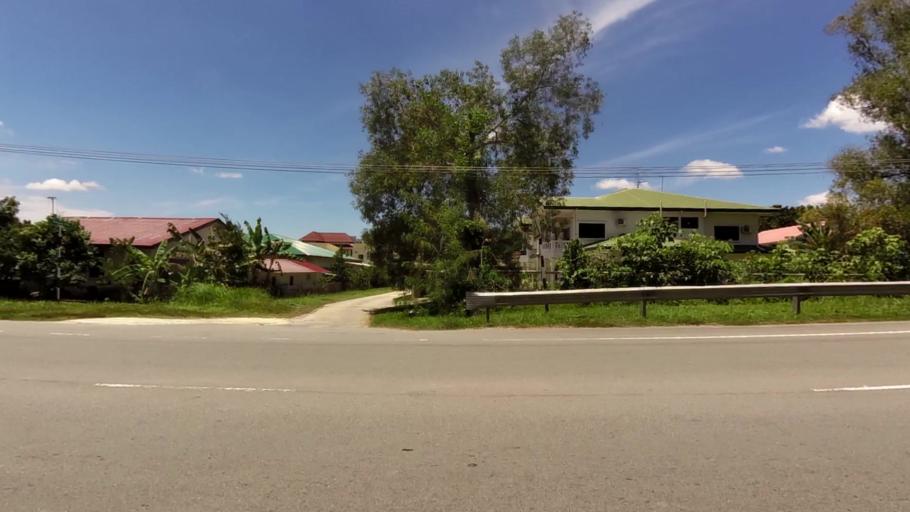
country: BN
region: Brunei and Muara
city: Bandar Seri Begawan
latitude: 4.9316
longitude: 114.9591
